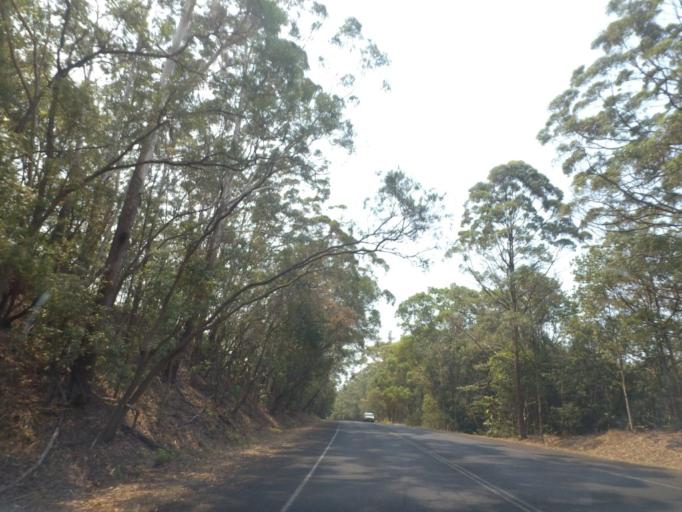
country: AU
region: New South Wales
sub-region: Byron Shire
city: Brunswick Heads
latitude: -28.5095
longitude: 153.5321
